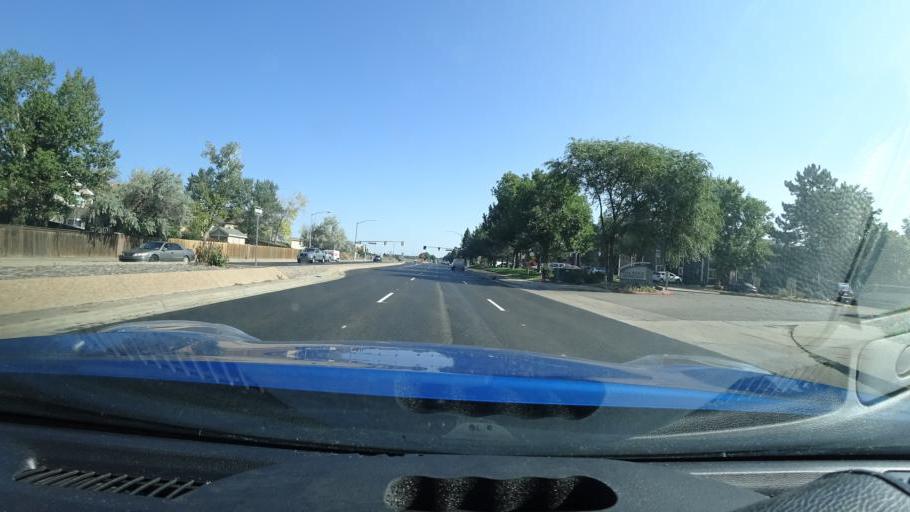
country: US
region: Colorado
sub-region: Adams County
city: Aurora
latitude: 39.7027
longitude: -104.8098
